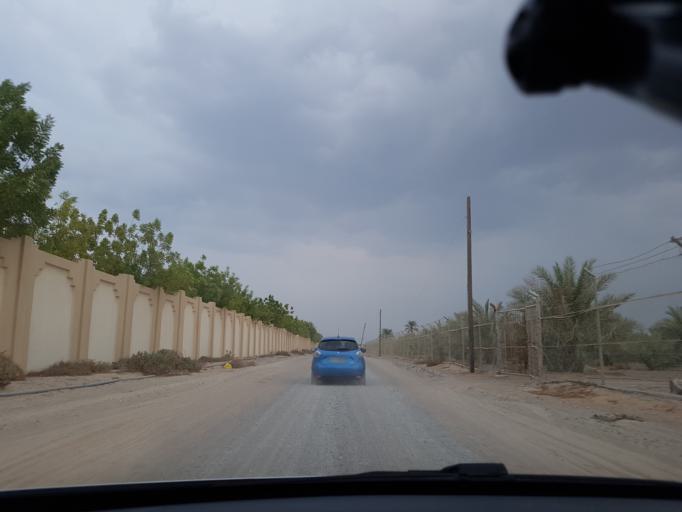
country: AE
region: Ash Shariqah
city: Adh Dhayd
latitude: 25.2757
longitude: 55.9154
